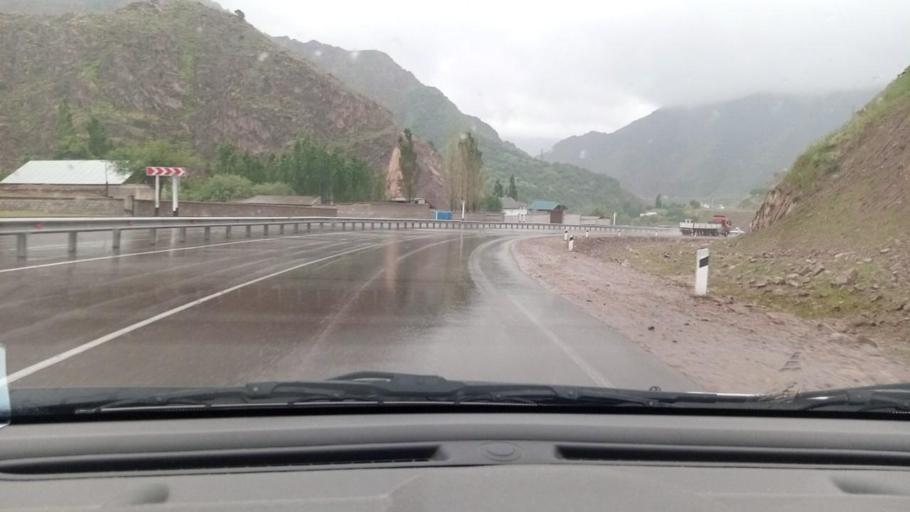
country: UZ
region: Toshkent
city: Angren
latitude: 41.1052
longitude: 70.3344
